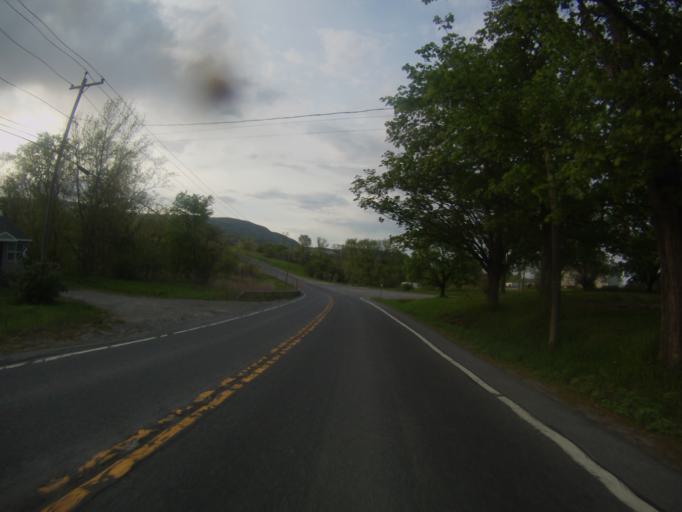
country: US
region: New York
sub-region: Essex County
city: Ticonderoga
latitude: 43.8647
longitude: -73.4372
